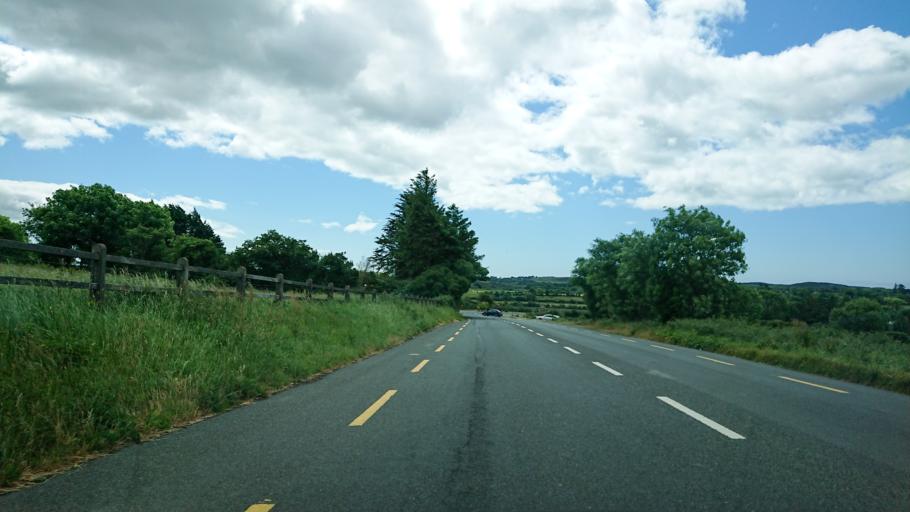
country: IE
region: Munster
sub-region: Waterford
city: Tra Mhor
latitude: 52.2000
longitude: -7.1941
